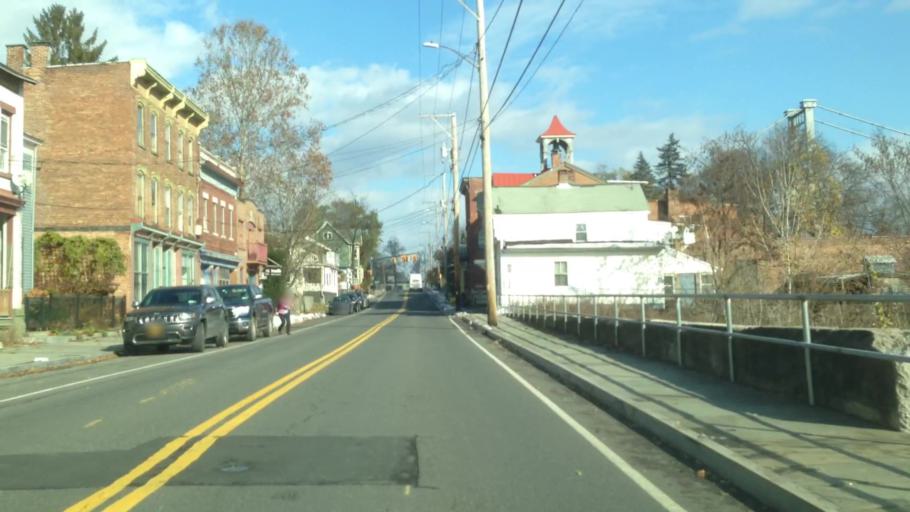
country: US
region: New York
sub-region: Ulster County
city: Kingston
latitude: 41.9166
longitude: -73.9870
